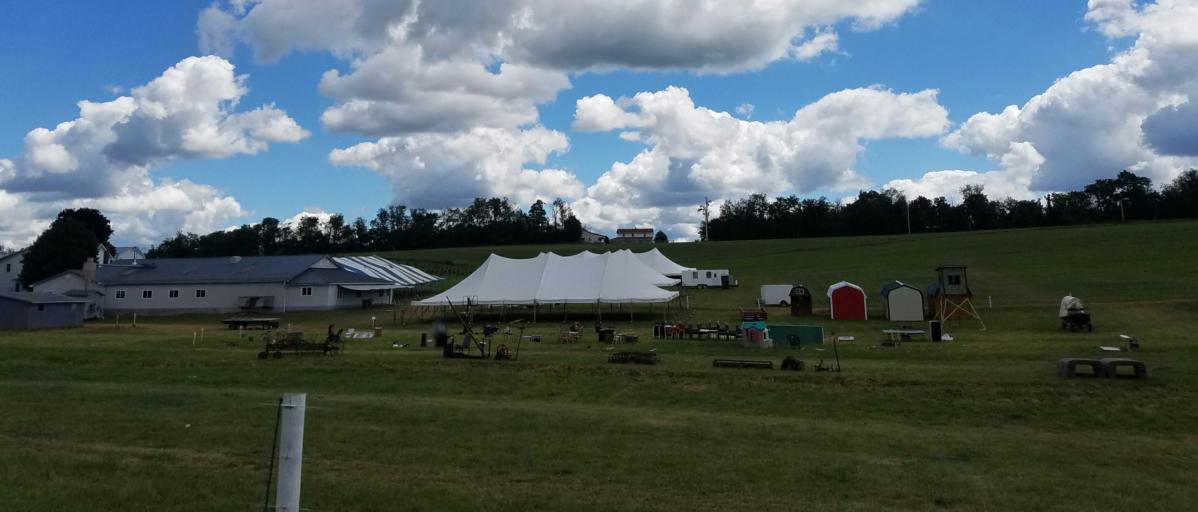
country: US
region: Ohio
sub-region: Knox County
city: Danville
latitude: 40.5376
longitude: -82.3604
